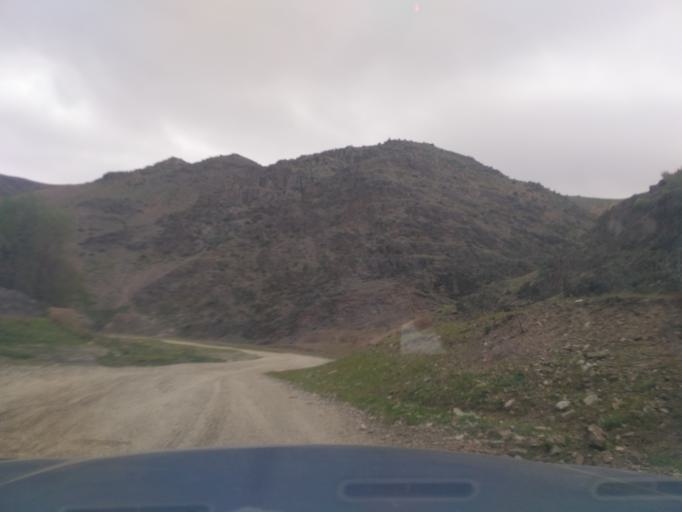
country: UZ
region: Jizzax
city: Zomin
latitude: 39.8512
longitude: 68.3956
